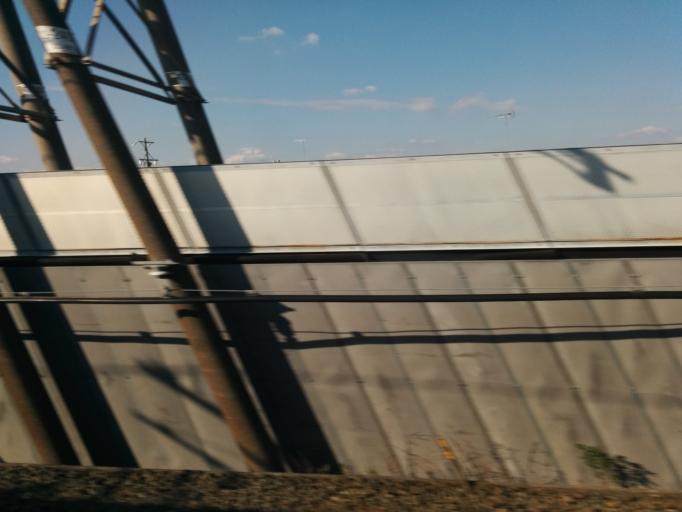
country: JP
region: Shizuoka
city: Iwata
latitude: 34.7104
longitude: 137.8746
